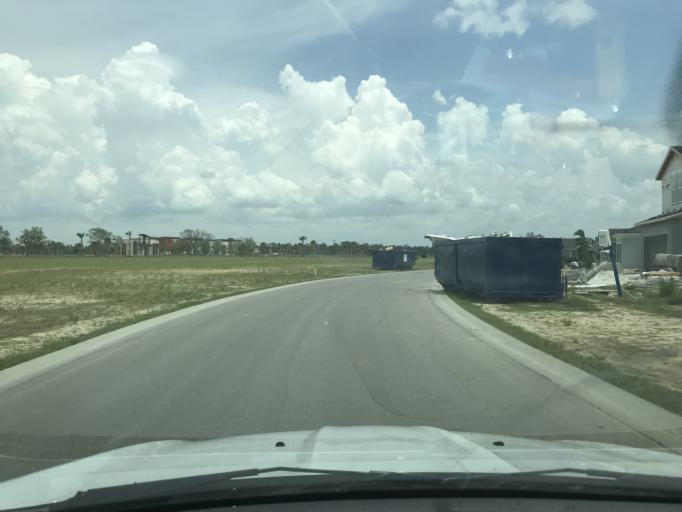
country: US
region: Florida
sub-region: Lee County
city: Olga
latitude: 26.7818
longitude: -81.7436
